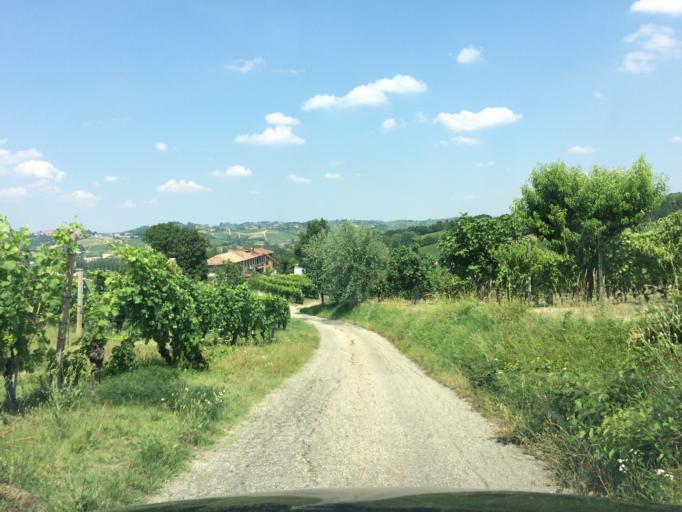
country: IT
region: Piedmont
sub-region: Provincia di Asti
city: Moasca
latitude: 44.7652
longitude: 8.2638
